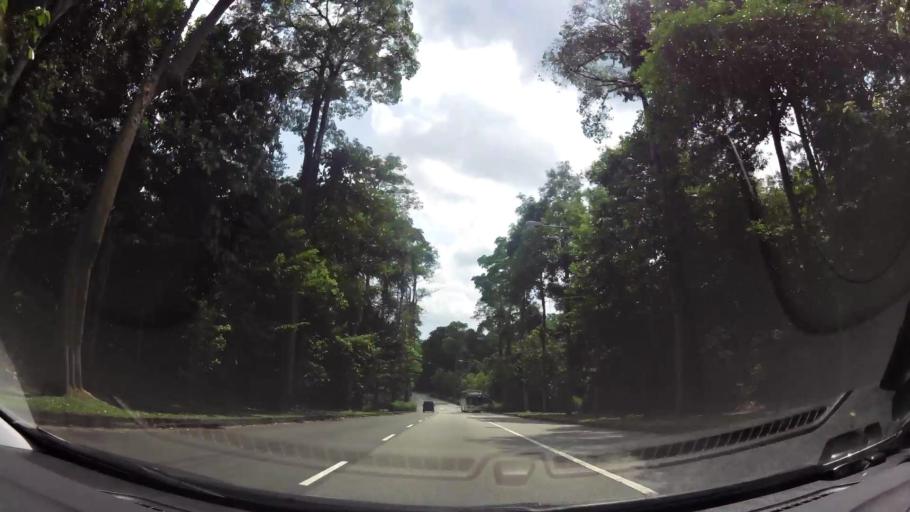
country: MY
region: Johor
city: Johor Bahru
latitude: 1.4052
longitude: 103.7861
